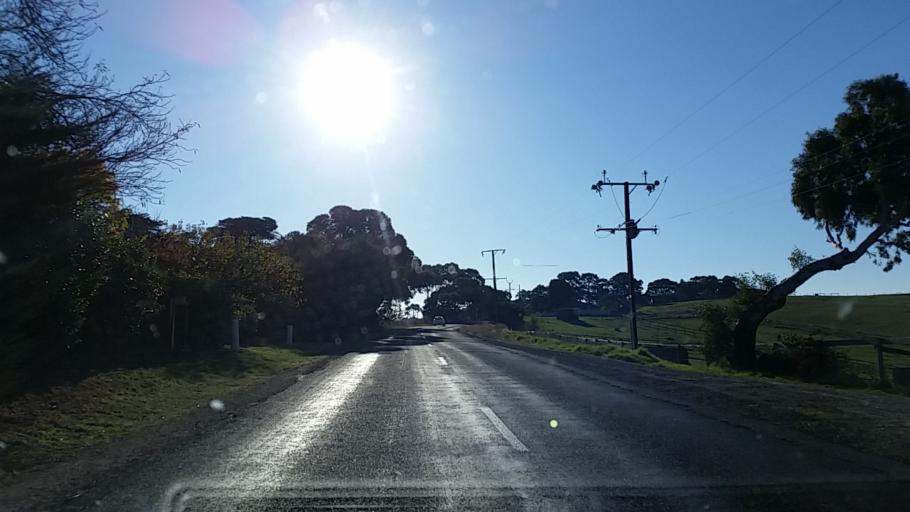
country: AU
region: South Australia
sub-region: Mount Barker
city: Mount Barker
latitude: -35.1188
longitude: 138.8961
